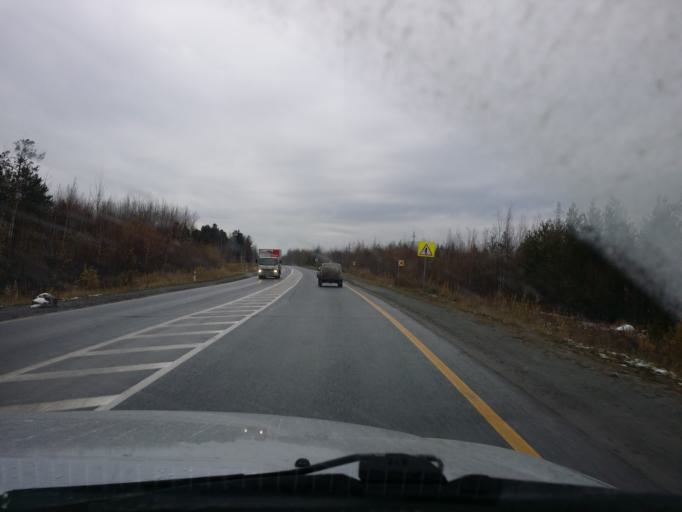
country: RU
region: Khanty-Mansiyskiy Avtonomnyy Okrug
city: Megion
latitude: 61.1071
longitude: 75.9030
